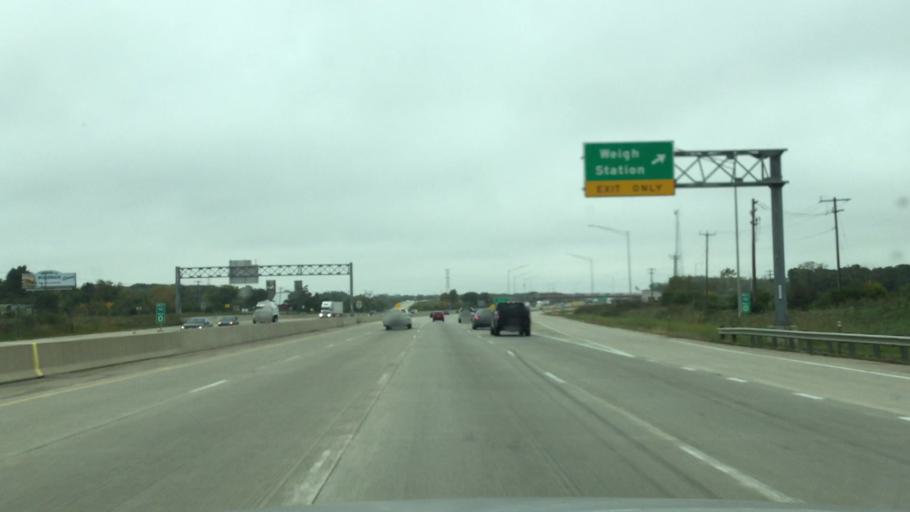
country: US
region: Wisconsin
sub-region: Kenosha County
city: Pleasant Prairie
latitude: 42.4944
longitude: -87.9497
